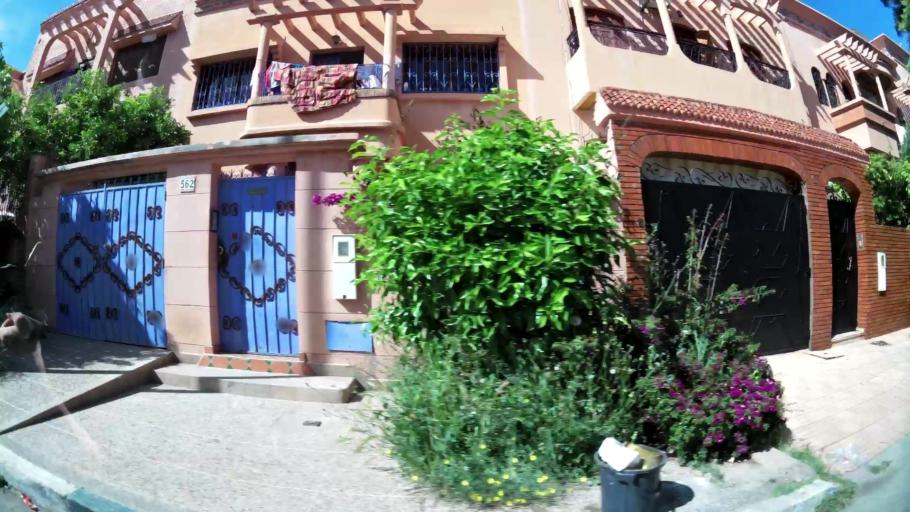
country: MA
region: Marrakech-Tensift-Al Haouz
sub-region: Marrakech
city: Marrakesh
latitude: 31.6563
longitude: -8.0566
